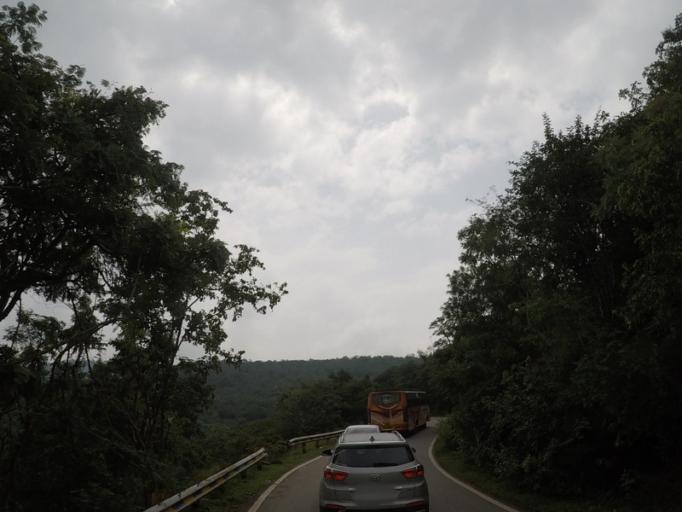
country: IN
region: Karnataka
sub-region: Chikmagalur
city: Birur
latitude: 13.5447
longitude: 75.8217
